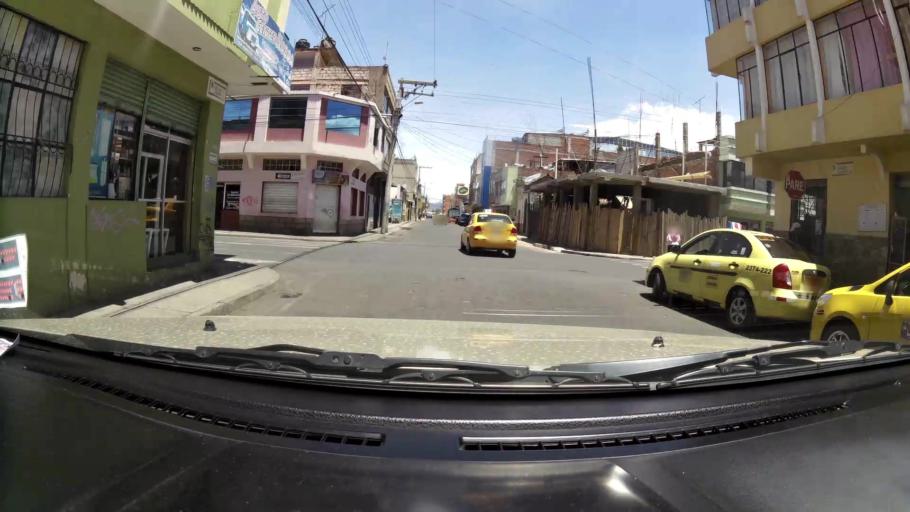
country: EC
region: Chimborazo
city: Riobamba
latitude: -1.6758
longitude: -78.6455
